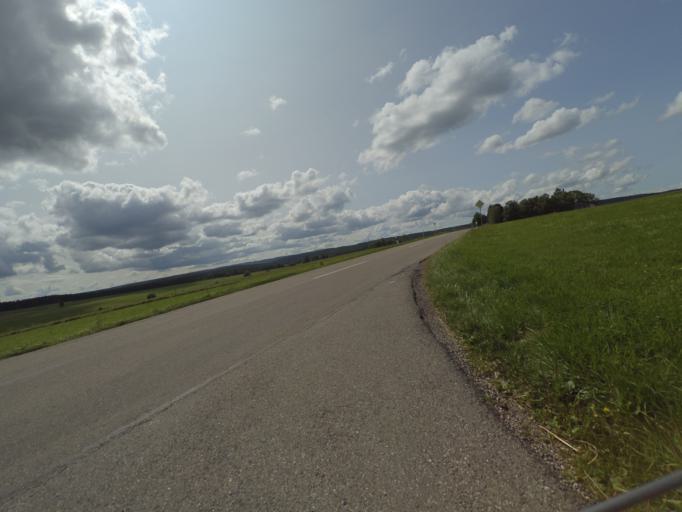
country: DE
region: Baden-Wuerttemberg
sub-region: Freiburg Region
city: Loffingen
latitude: 47.8912
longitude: 8.3110
